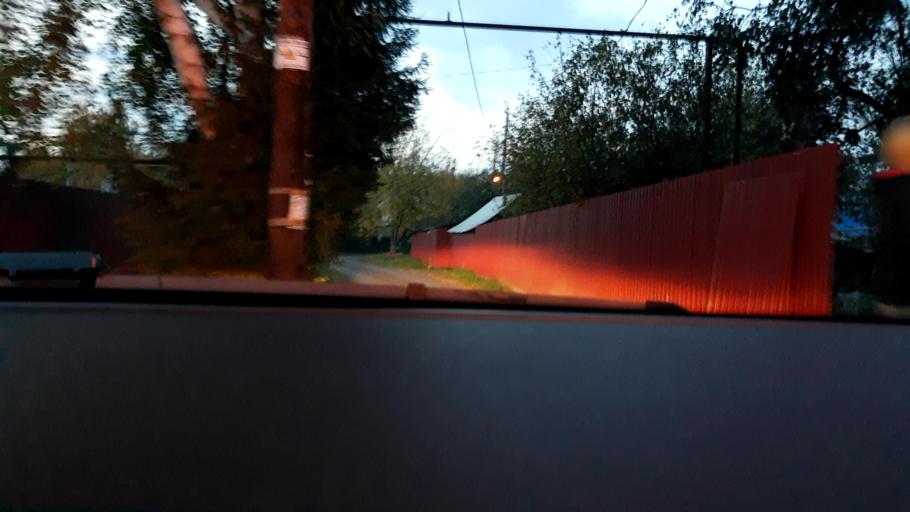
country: RU
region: Nizjnij Novgorod
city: Nizhniy Novgorod
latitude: 56.3343
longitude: 43.9132
